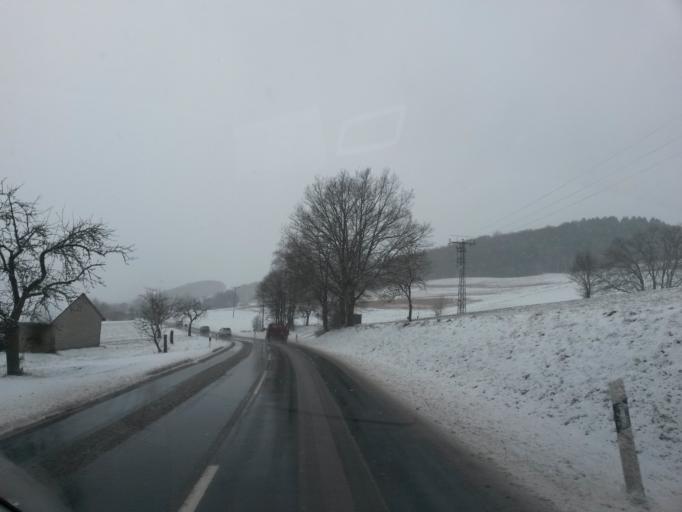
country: DE
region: Hesse
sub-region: Regierungsbezirk Kassel
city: Poppenhausen
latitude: 50.4927
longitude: 9.8429
